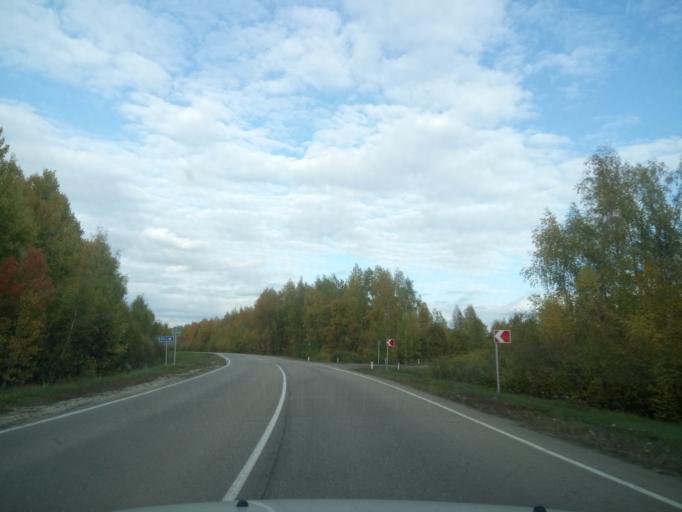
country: RU
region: Nizjnij Novgorod
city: Bol'shoye Boldino
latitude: 54.9184
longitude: 45.1618
